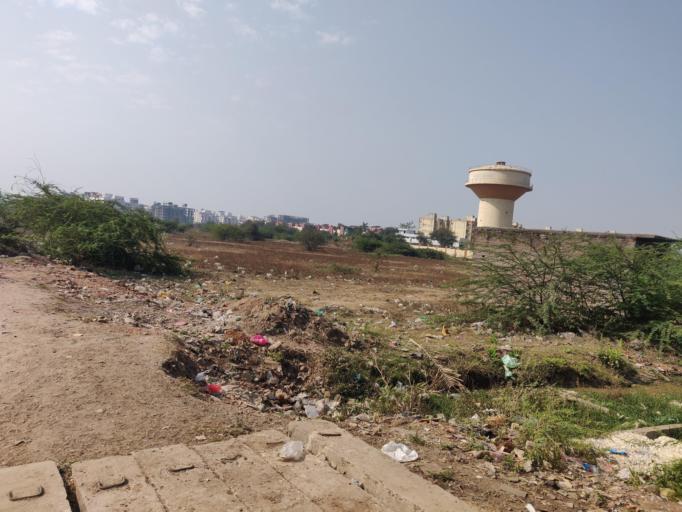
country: IN
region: Gujarat
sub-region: Vadodara
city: Vadodara
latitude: 22.2926
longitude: 73.2486
